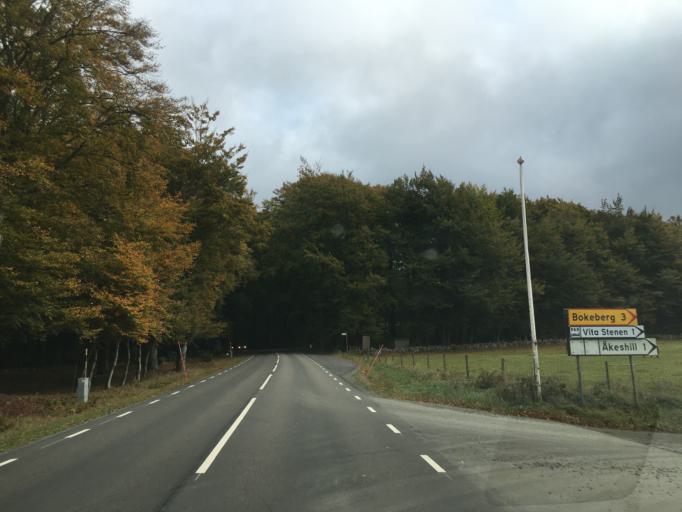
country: SE
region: Skane
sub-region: Tomelilla Kommun
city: Tomelilla
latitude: 55.6340
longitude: 14.0909
